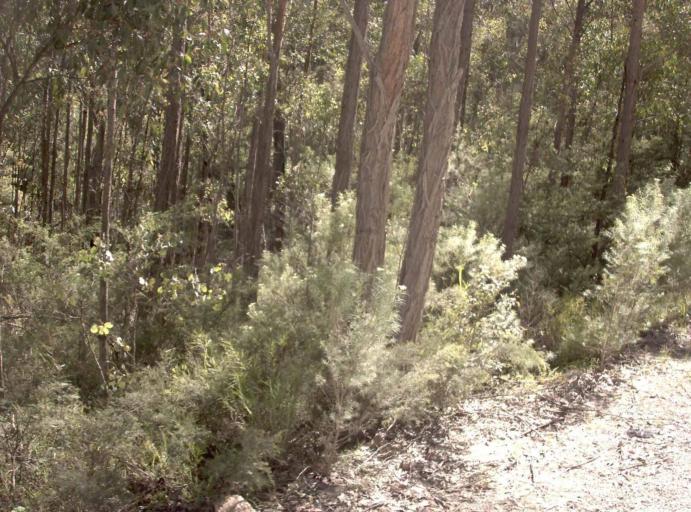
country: AU
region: Victoria
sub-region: East Gippsland
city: Lakes Entrance
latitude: -37.3913
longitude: 148.1242
